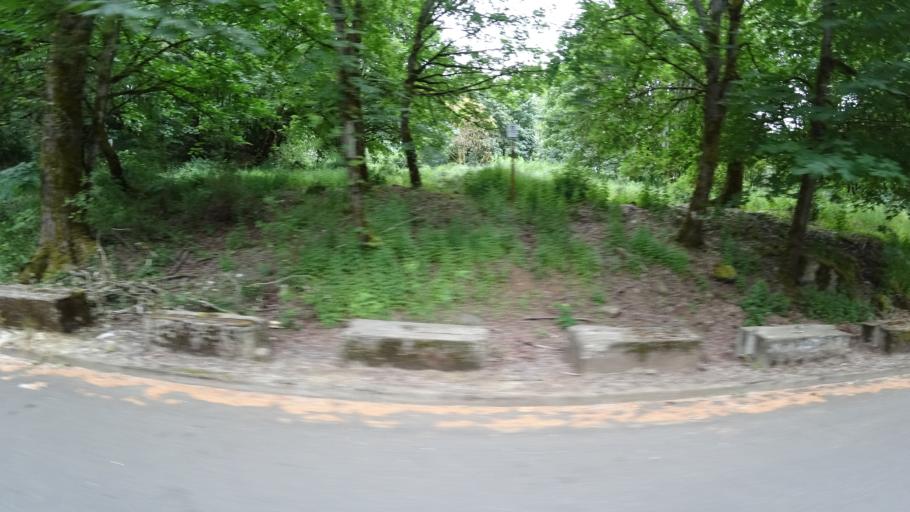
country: US
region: Oregon
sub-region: Multnomah County
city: Lents
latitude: 45.4694
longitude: -122.5607
